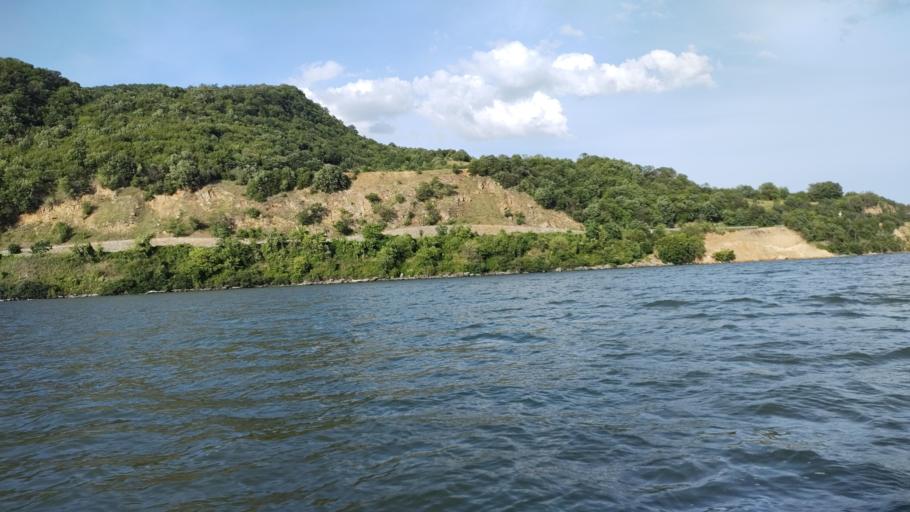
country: RO
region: Mehedinti
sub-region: Comuna Svinita
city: Svinita
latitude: 44.4832
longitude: 22.1201
